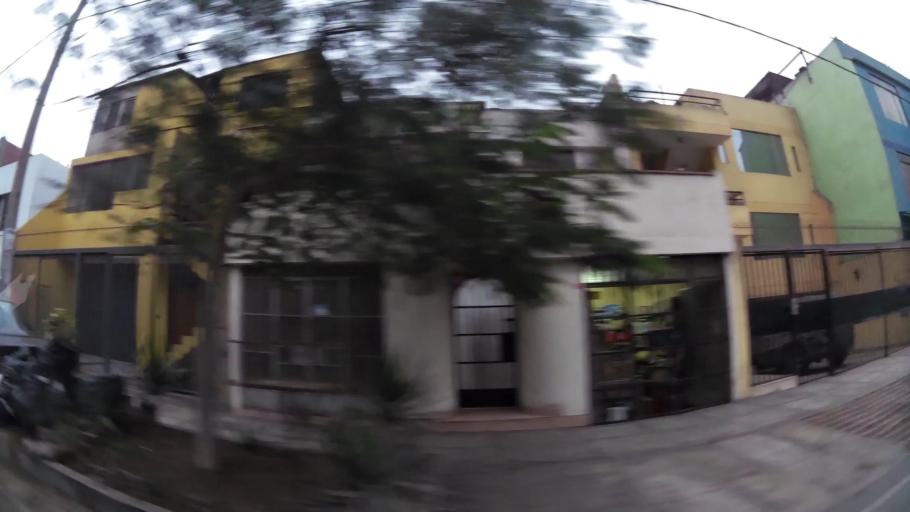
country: PE
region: Lima
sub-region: Lima
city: La Molina
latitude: -12.1157
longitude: -76.9388
